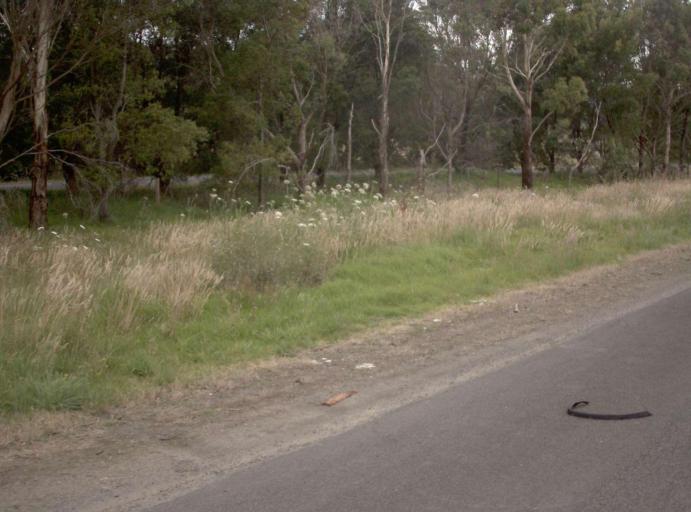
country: AU
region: Victoria
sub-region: Latrobe
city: Moe
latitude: -38.1884
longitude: 146.2251
